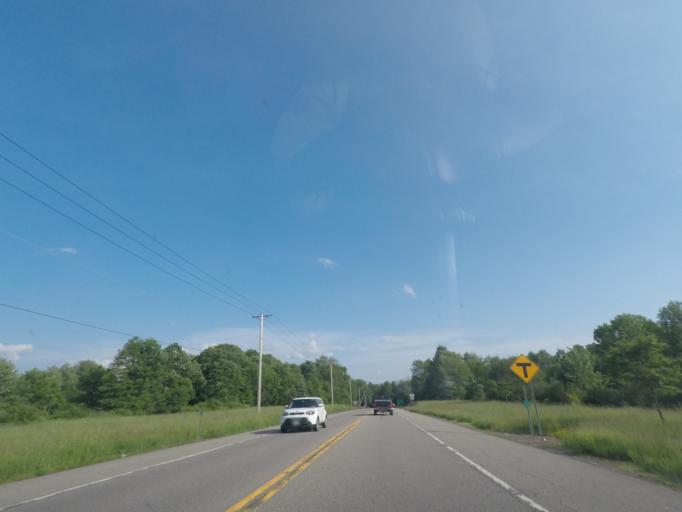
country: US
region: New York
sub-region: Orange County
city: Beaverdam Lake-Salisbury Mills
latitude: 41.4807
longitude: -74.1303
